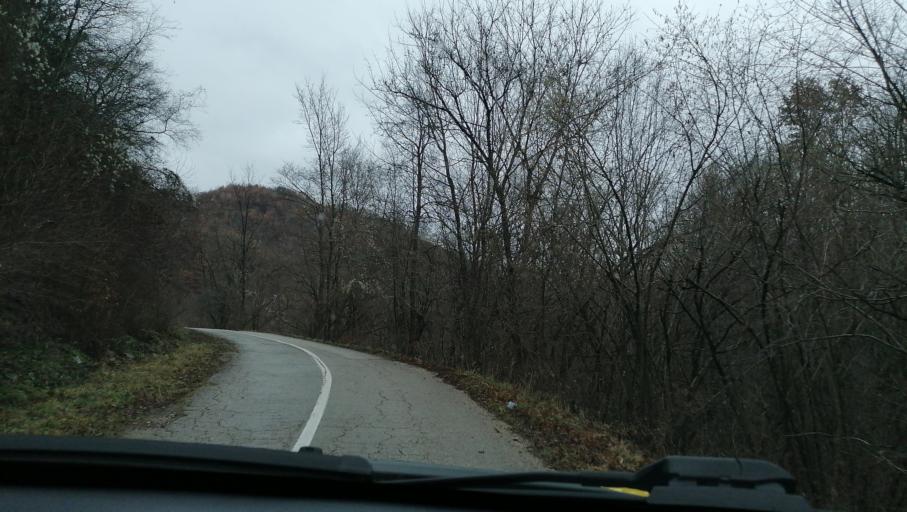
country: RS
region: Central Serbia
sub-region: Pirotski Okrug
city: Dimitrovgrad
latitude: 42.9758
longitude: 22.7853
